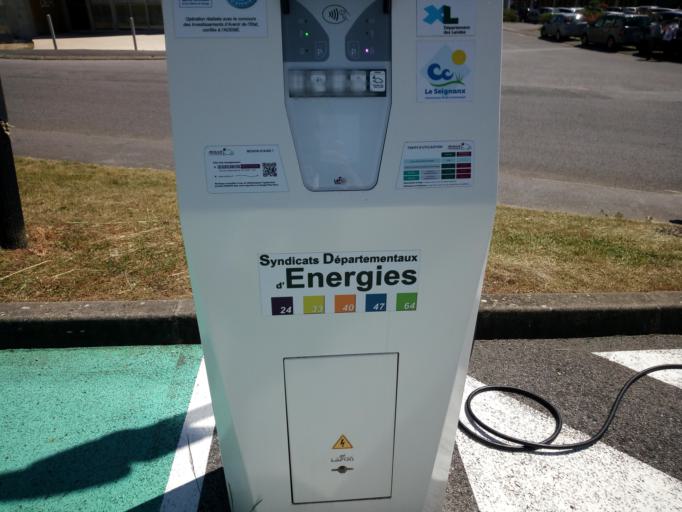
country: FR
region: Aquitaine
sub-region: Departement des Landes
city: Tarnos
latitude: 43.5456
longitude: -1.4918
